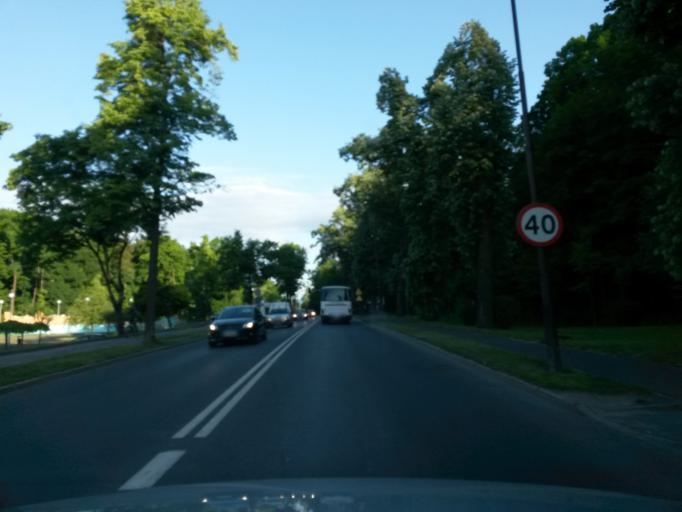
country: PL
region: Lower Silesian Voivodeship
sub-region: Jelenia Gora
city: Jelenia Gora
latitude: 50.8942
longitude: 15.7455
